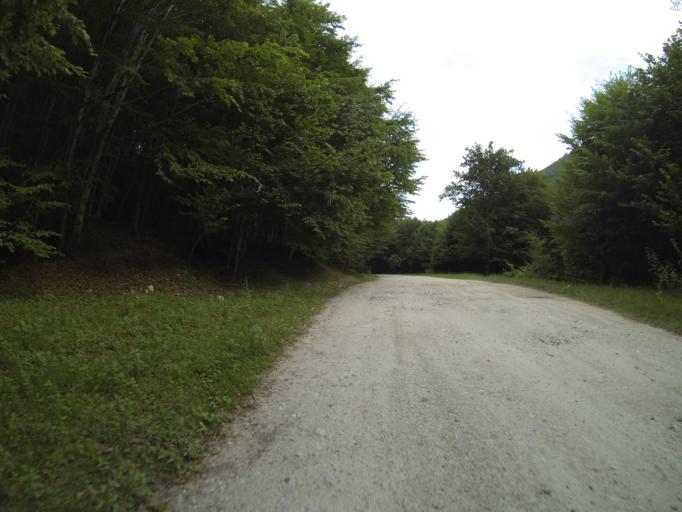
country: RO
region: Gorj
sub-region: Comuna Polovragi
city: Polovragi
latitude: 45.2255
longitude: 23.7716
